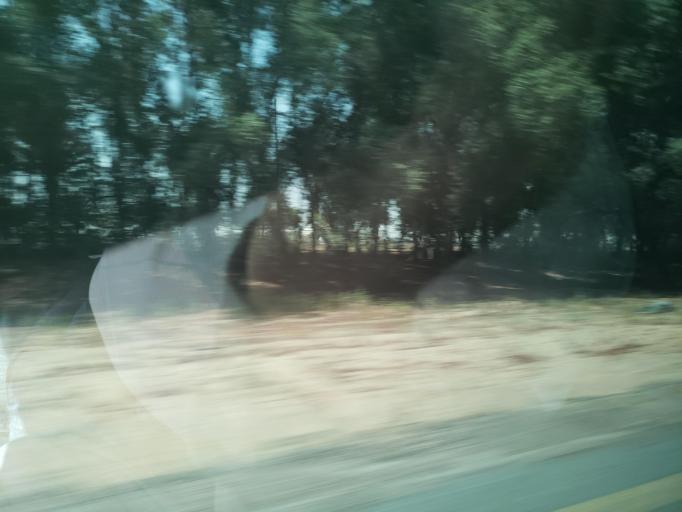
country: AE
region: Ash Shariqah
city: Sharjah
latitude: 25.3235
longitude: 55.4979
